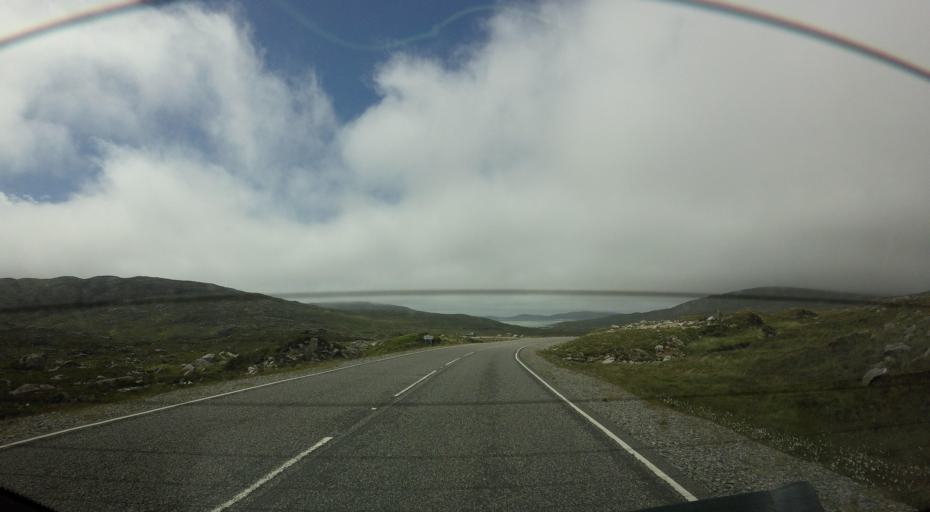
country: GB
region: Scotland
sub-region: Eilean Siar
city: Harris
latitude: 57.8603
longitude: -6.8654
